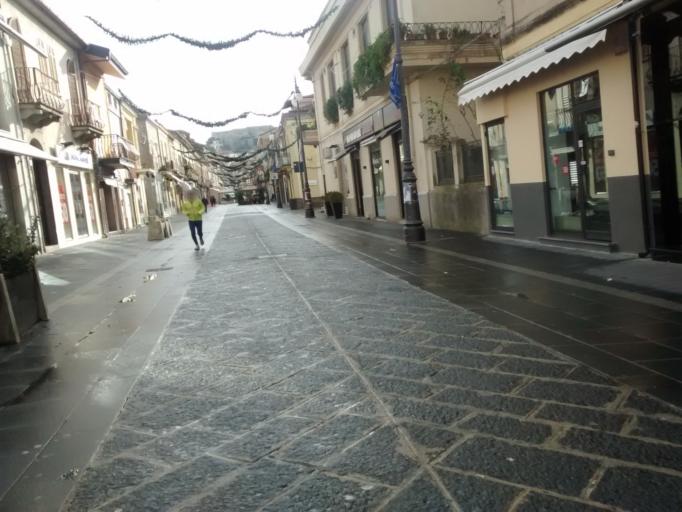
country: IT
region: Calabria
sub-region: Provincia di Vibo-Valentia
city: Vibo Valentia
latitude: 38.6744
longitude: 16.0995
